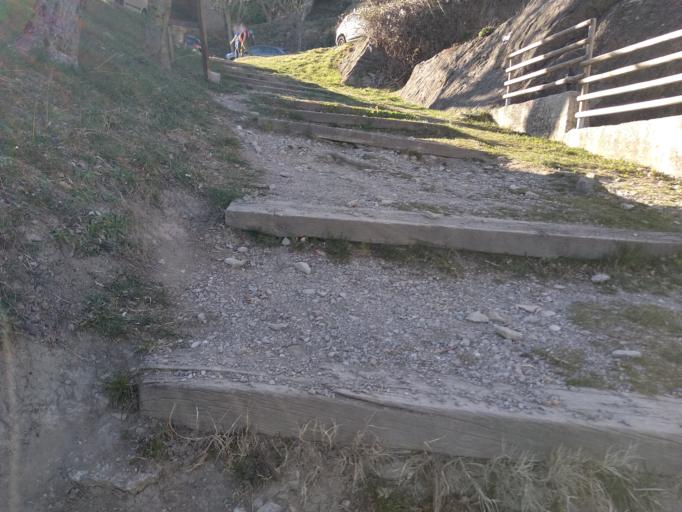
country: IT
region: Emilia-Romagna
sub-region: Provincia di Reggio Emilia
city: Castelnovo ne'Monti
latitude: 44.4177
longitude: 10.4124
